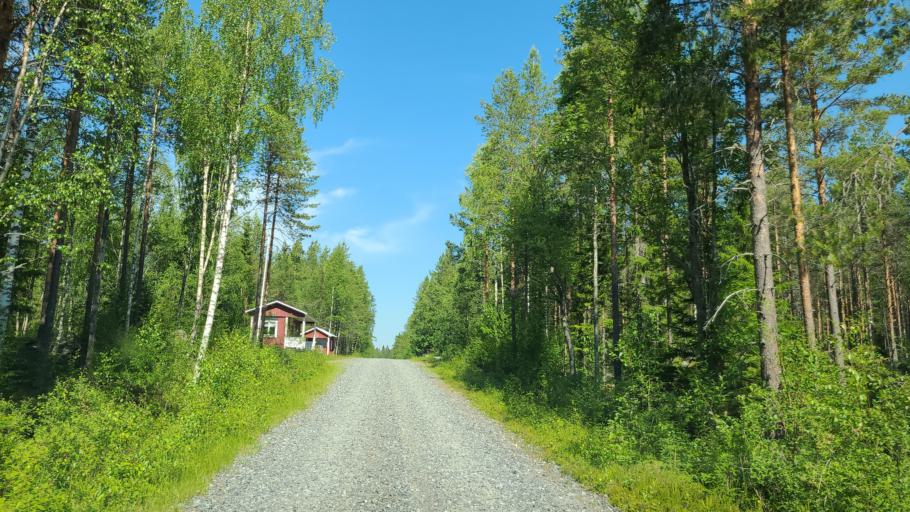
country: SE
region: Vaesterbotten
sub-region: Robertsfors Kommun
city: Robertsfors
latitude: 64.0954
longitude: 20.8345
